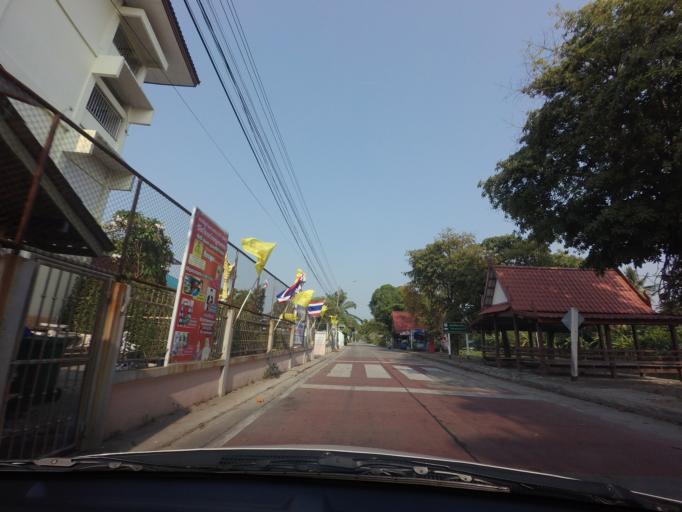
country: TH
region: Nonthaburi
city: Bang Yai
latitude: 13.8028
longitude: 100.3763
